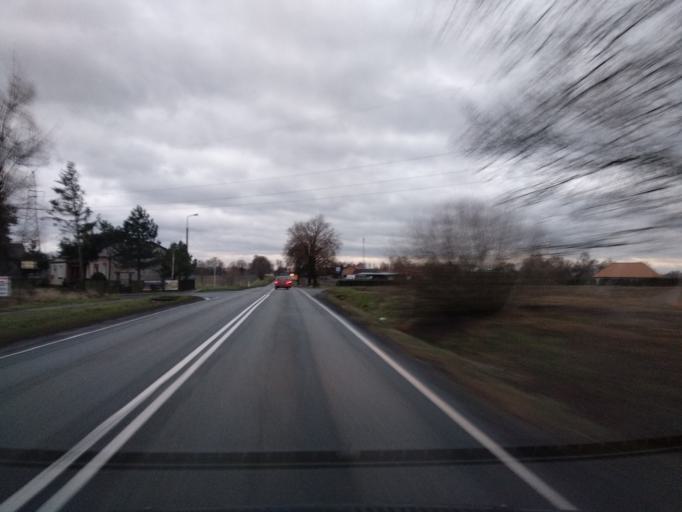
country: PL
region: Greater Poland Voivodeship
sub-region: Powiat koninski
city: Rychwal
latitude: 52.0817
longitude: 18.1614
